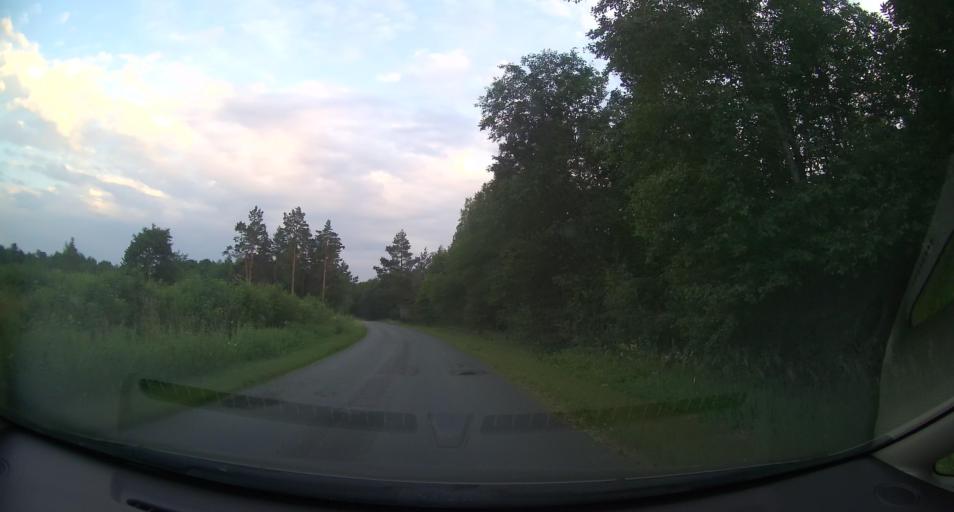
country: EE
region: Laeaene
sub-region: Lihula vald
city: Lihula
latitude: 58.5864
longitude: 23.6101
